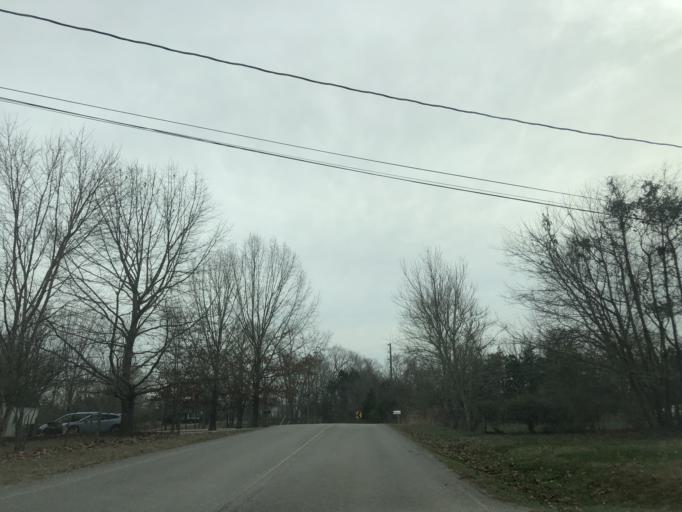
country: US
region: Tennessee
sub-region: Wilson County
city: Lebanon
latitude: 36.2454
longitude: -86.2608
